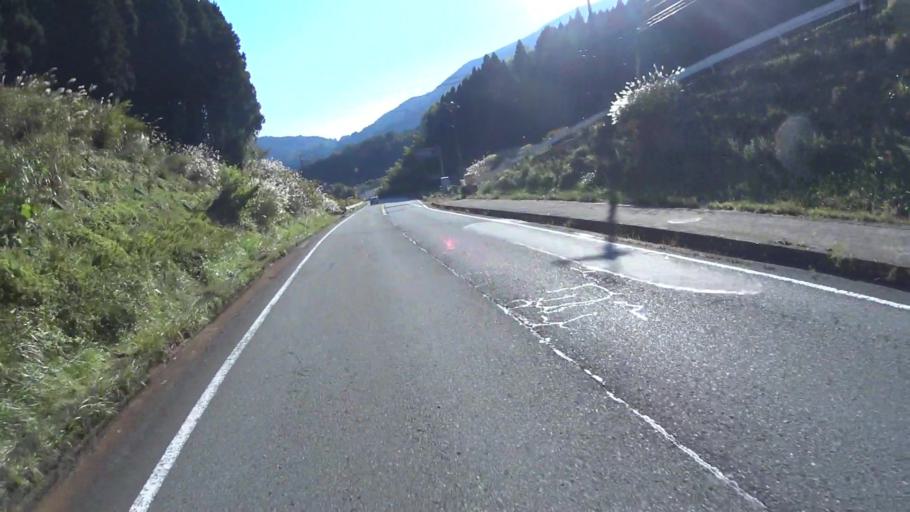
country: JP
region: Kyoto
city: Fukuchiyama
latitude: 35.4079
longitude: 135.0837
